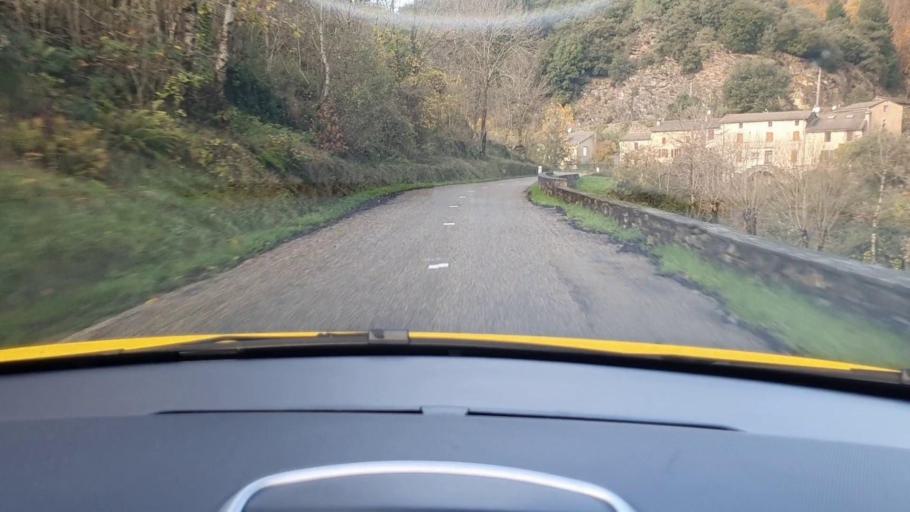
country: FR
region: Languedoc-Roussillon
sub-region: Departement du Gard
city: Valleraugue
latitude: 44.1693
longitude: 3.6479
